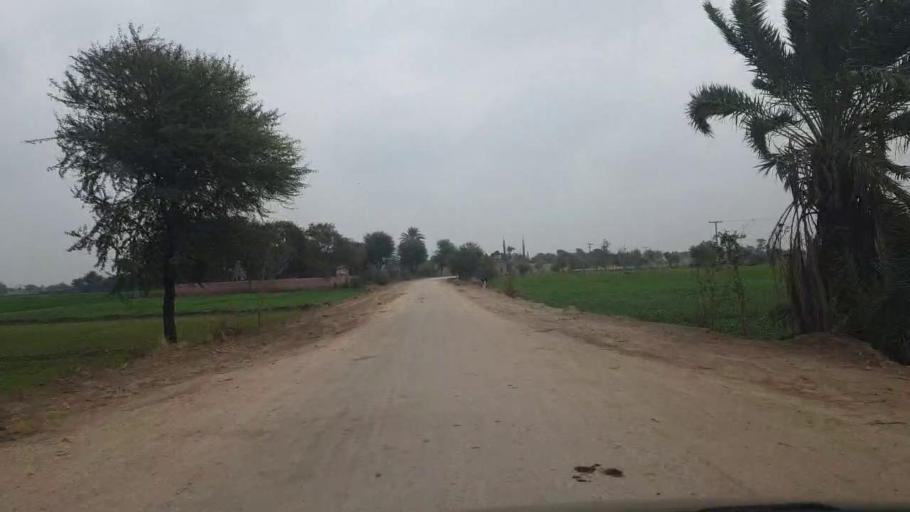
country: PK
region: Sindh
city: Shahdadpur
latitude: 25.8667
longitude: 68.6916
